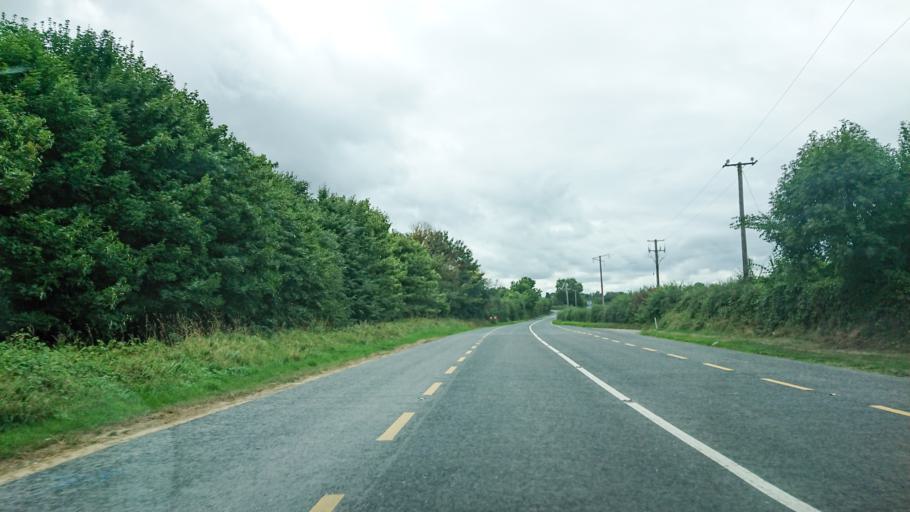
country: IE
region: Munster
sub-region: County Cork
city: Mallow
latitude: 52.1526
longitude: -8.5918
